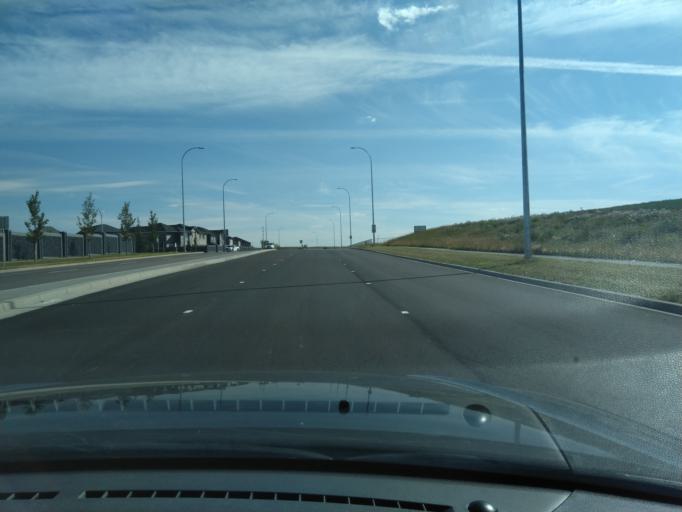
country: CA
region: Alberta
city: Calgary
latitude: 51.1769
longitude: -114.1761
